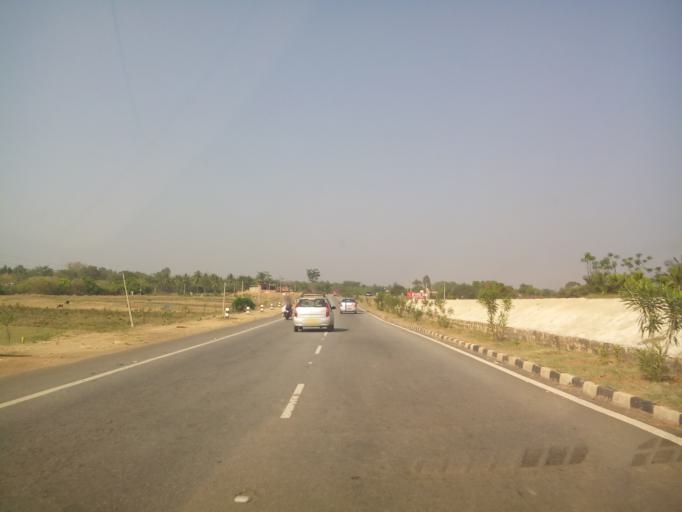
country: IN
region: Karnataka
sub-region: Tumkur
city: Kunigal
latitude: 13.0441
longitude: 77.1351
